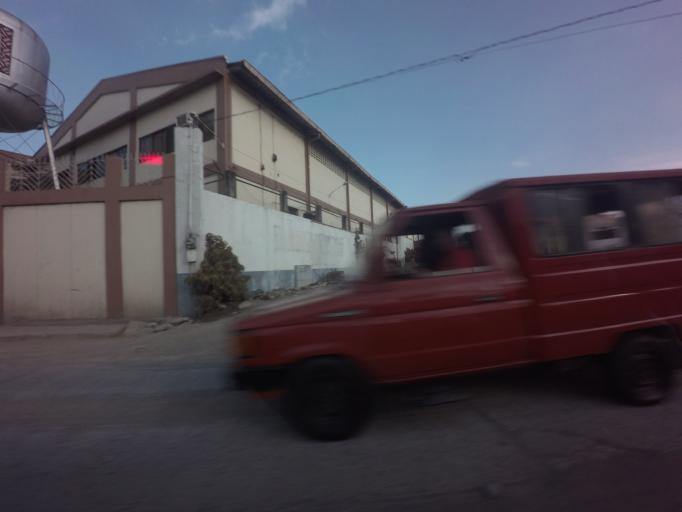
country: PH
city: Sambayanihan People's Village
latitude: 14.4972
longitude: 121.0021
